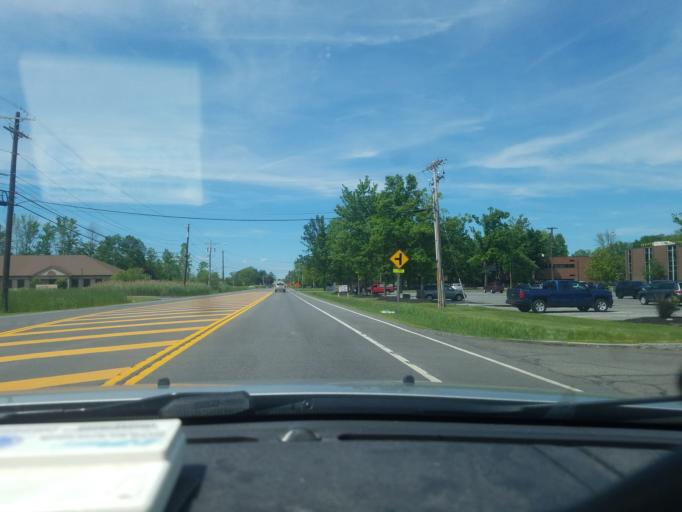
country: US
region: New York
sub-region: Onondaga County
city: East Syracuse
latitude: 43.0786
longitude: -76.0583
